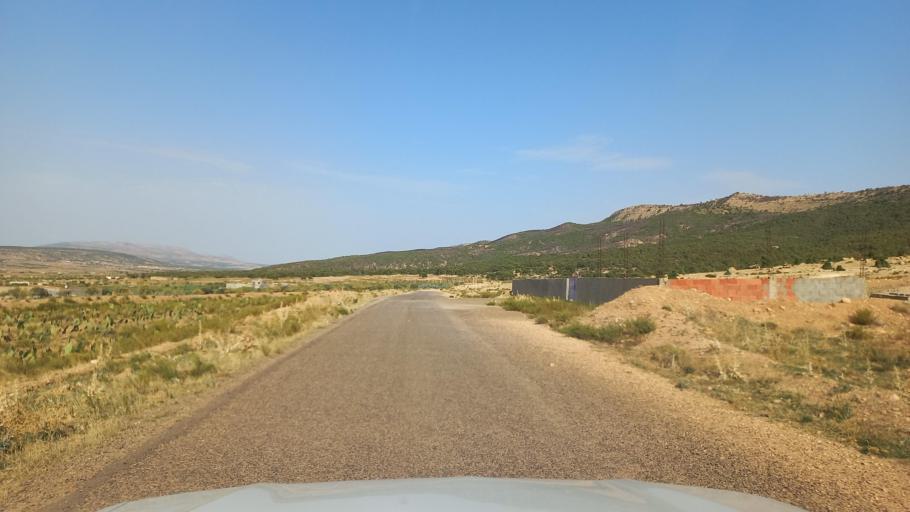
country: TN
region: Al Qasrayn
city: Kasserine
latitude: 35.3330
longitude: 8.8442
